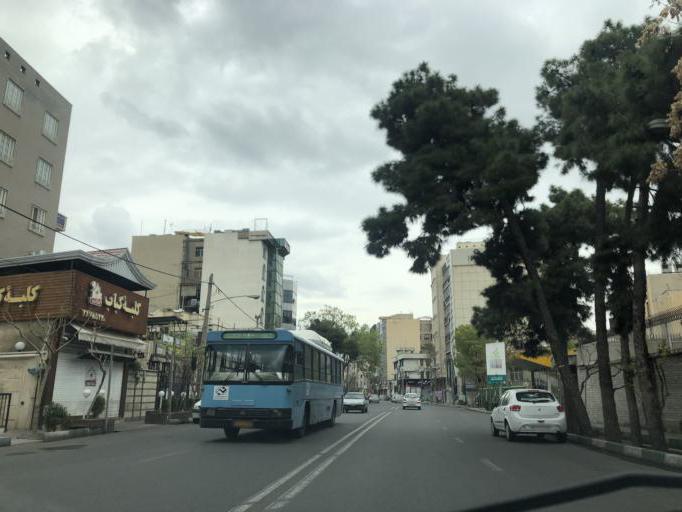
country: IR
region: Tehran
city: Tajrish
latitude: 35.7801
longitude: 51.4586
